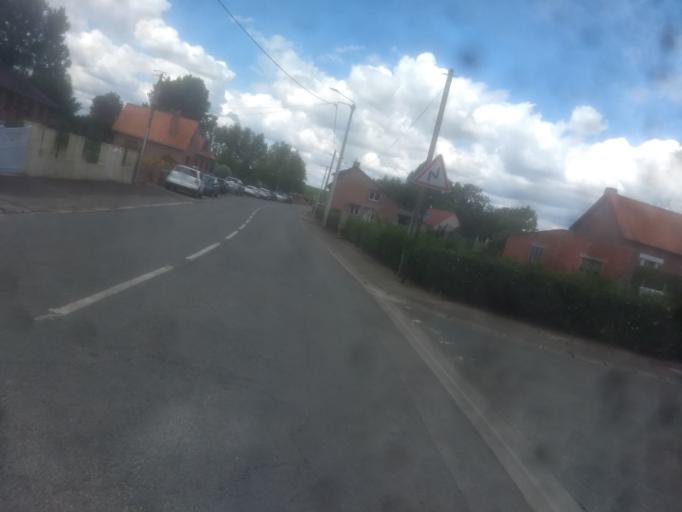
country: FR
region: Nord-Pas-de-Calais
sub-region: Departement du Pas-de-Calais
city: Beaurains
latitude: 50.2145
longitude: 2.8198
